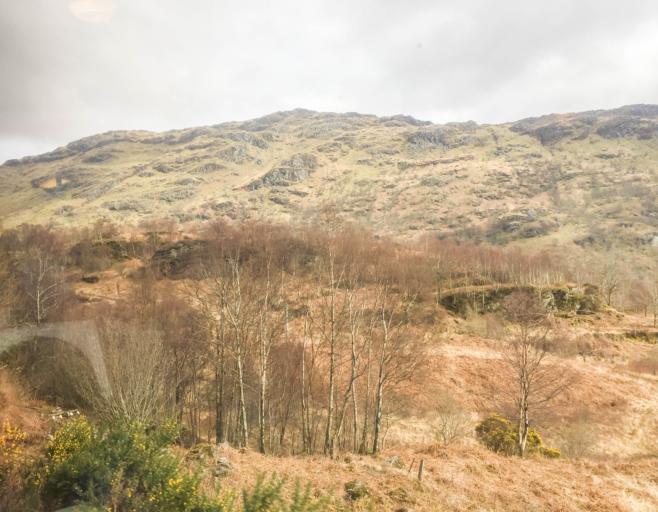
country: GB
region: Scotland
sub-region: Argyll and Bute
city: Garelochhead
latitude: 56.2802
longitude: -4.7055
